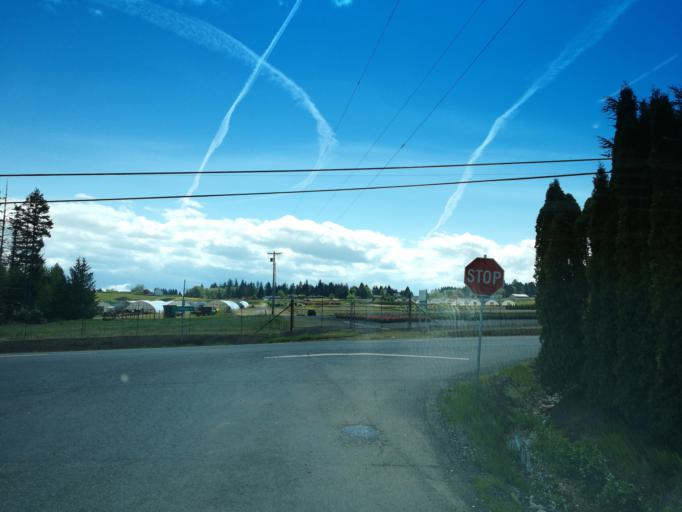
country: US
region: Oregon
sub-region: Clackamas County
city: Damascus
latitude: 45.4399
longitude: -122.4242
